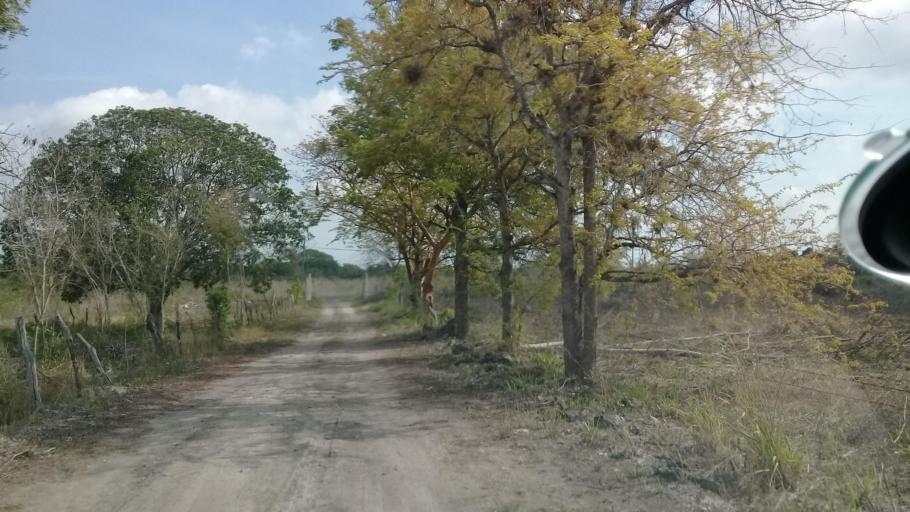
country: MX
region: Veracruz
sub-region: Emiliano Zapata
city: Plan del Rio
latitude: 19.3878
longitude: -96.6425
